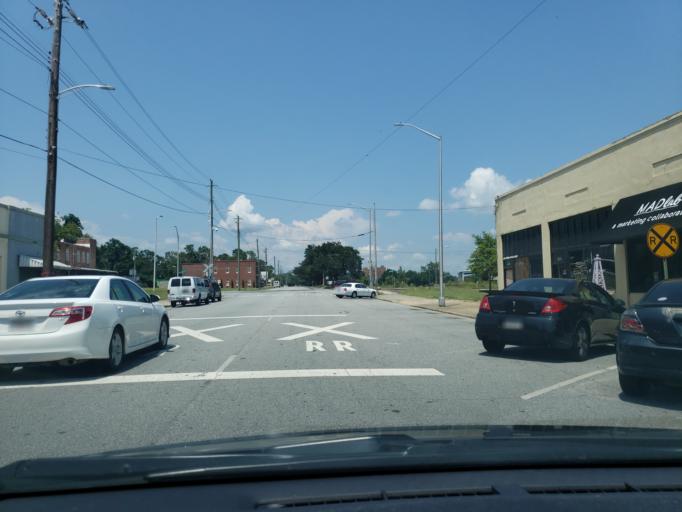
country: US
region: Georgia
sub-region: Dougherty County
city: Albany
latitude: 31.5808
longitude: -84.1514
